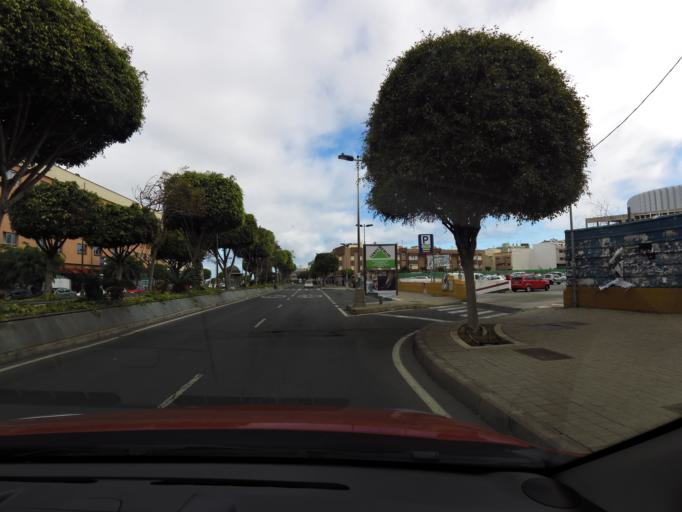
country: ES
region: Canary Islands
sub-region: Provincia de Las Palmas
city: Telde
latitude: 27.9989
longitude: -15.4191
